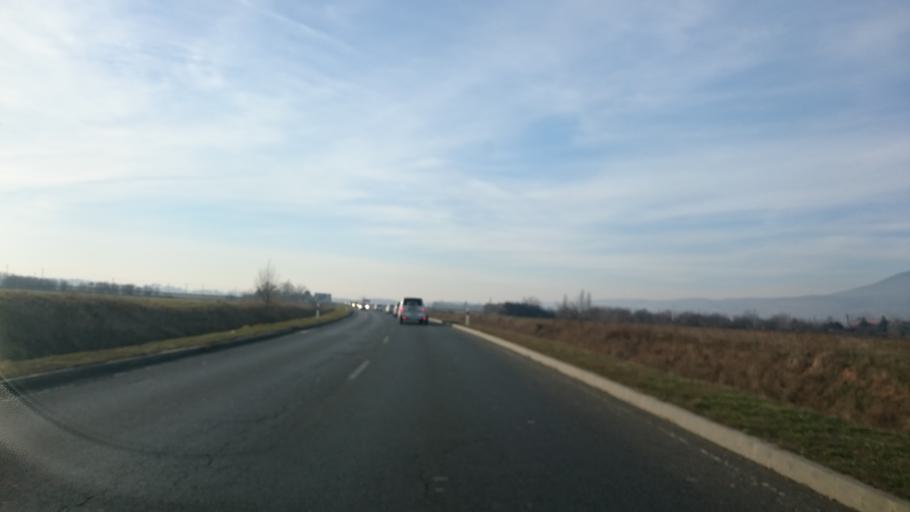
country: HU
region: Baranya
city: Pellerd
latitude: 46.0549
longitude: 18.1908
